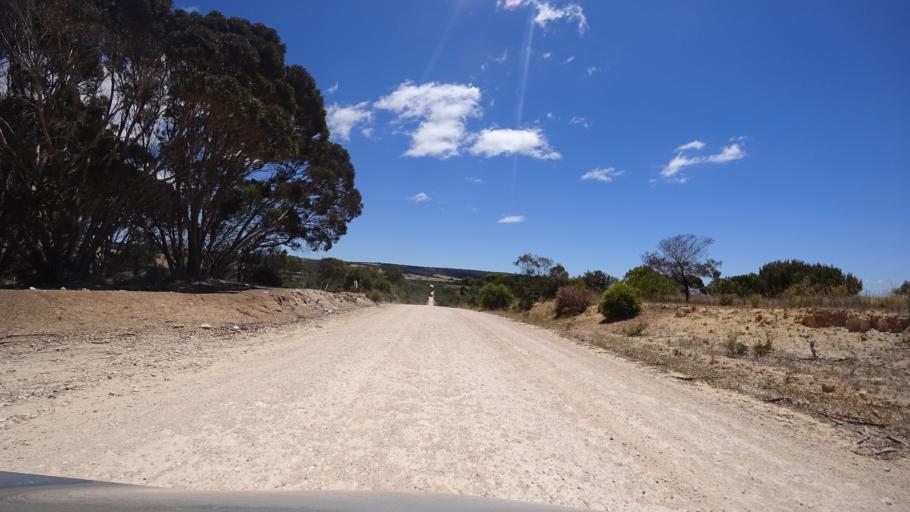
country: AU
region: South Australia
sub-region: Yankalilla
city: Normanville
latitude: -35.8110
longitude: 138.0724
